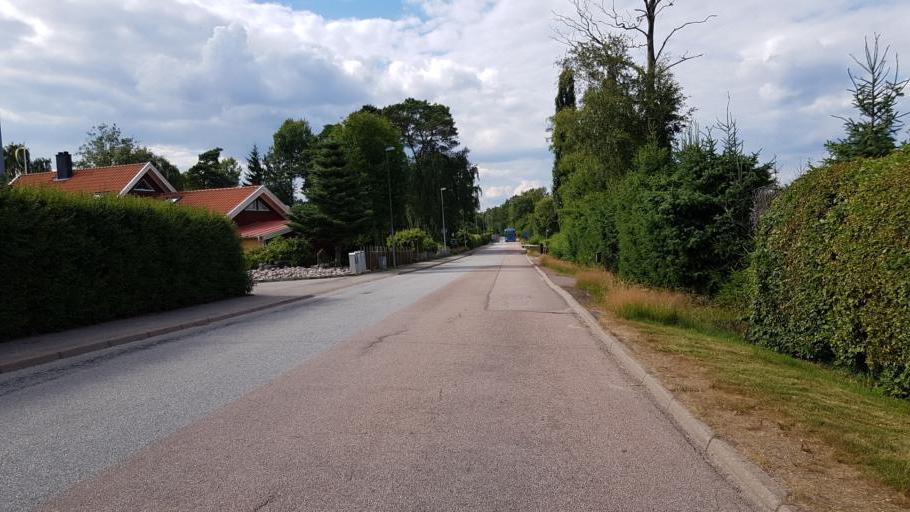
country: SE
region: Vaestra Goetaland
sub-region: Partille Kommun
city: Furulund
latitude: 57.7093
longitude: 12.1470
